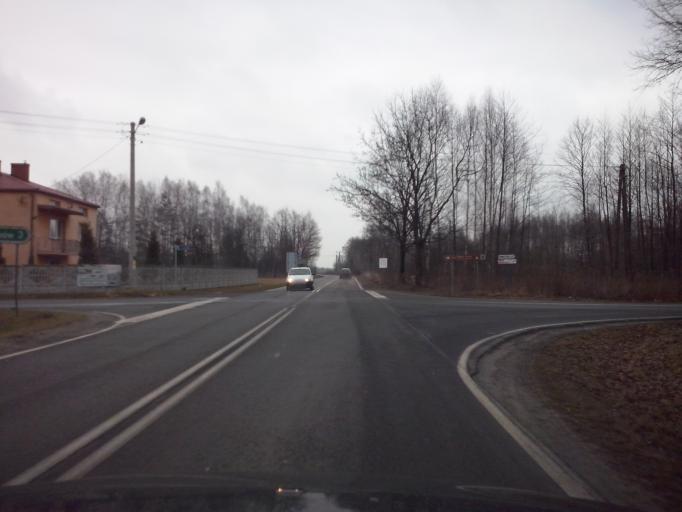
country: PL
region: Subcarpathian Voivodeship
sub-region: Powiat nizanski
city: Wolka Tanewska
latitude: 50.5166
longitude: 22.2635
